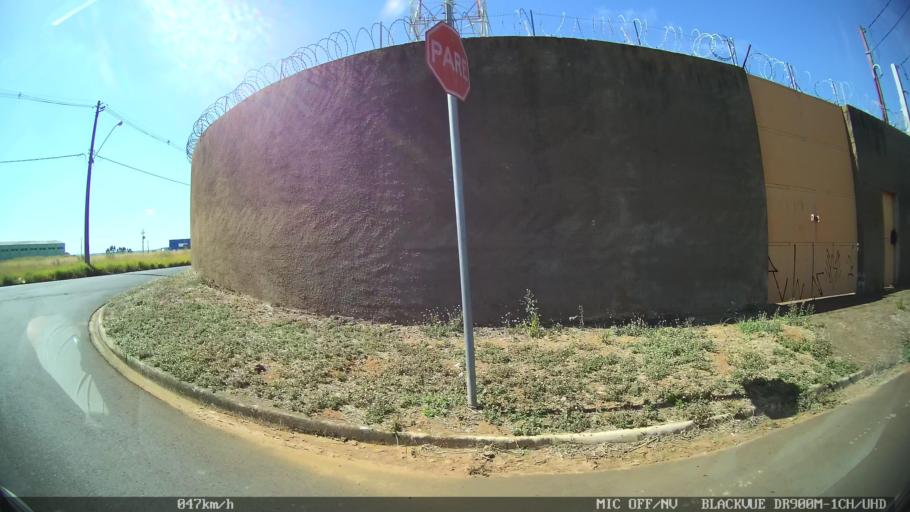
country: BR
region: Sao Paulo
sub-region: Franca
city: Franca
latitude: -20.5433
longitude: -47.4642
